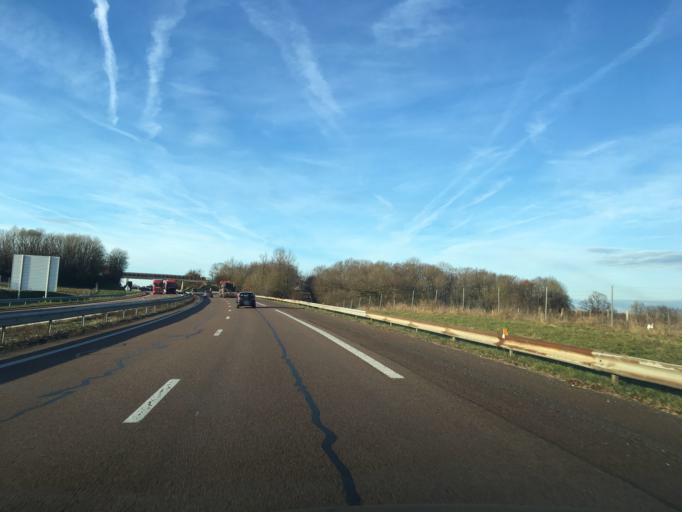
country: FR
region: Bourgogne
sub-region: Departement de l'Yonne
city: Avallon
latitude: 47.5571
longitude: 3.9505
